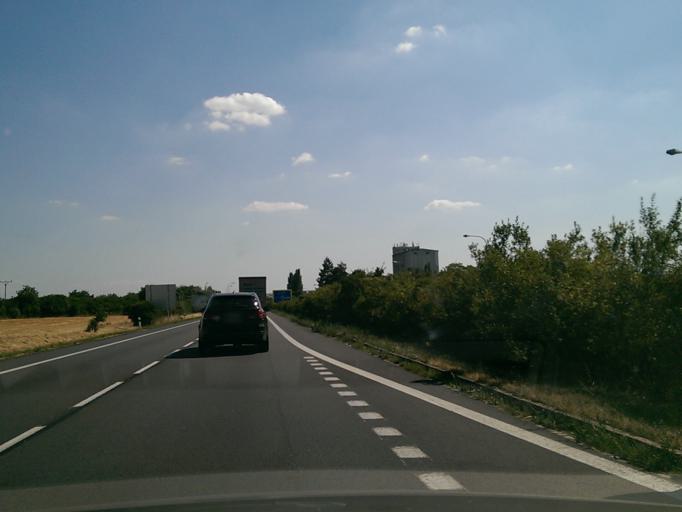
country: CZ
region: South Moravian
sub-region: Okres Breclav
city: Mikulov
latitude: 48.8117
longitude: 16.6255
